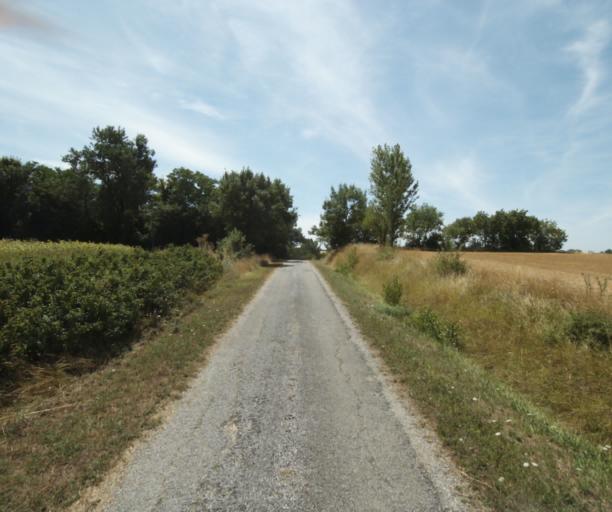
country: FR
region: Midi-Pyrenees
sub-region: Departement de la Haute-Garonne
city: Revel
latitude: 43.4930
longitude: 2.0286
